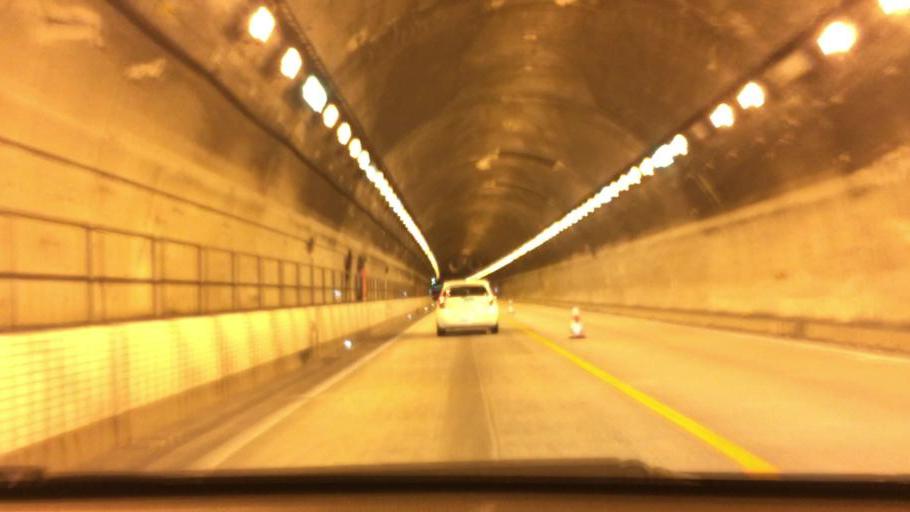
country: JP
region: Yamaguchi
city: Tokuyama
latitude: 34.0893
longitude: 131.7753
